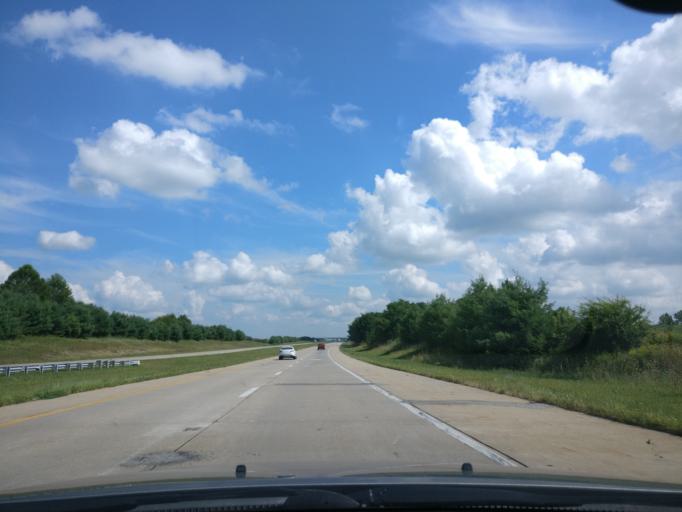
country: US
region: Ohio
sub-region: Greene County
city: Shawnee Hills
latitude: 39.6772
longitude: -83.8151
